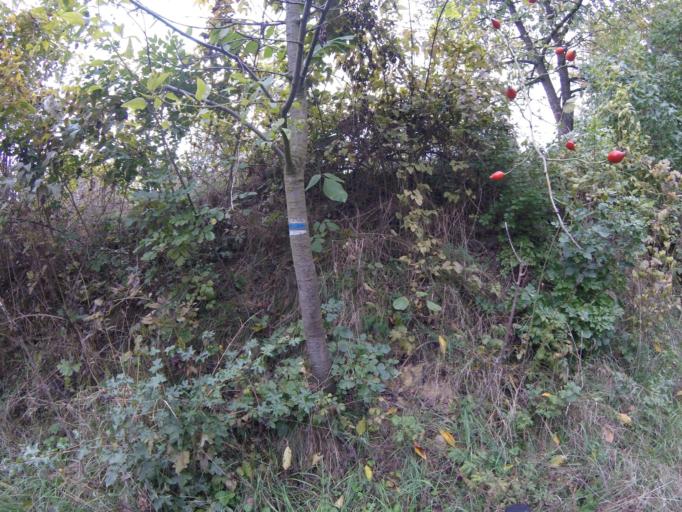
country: HU
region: Pest
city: Szob
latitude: 47.8286
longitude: 18.8145
